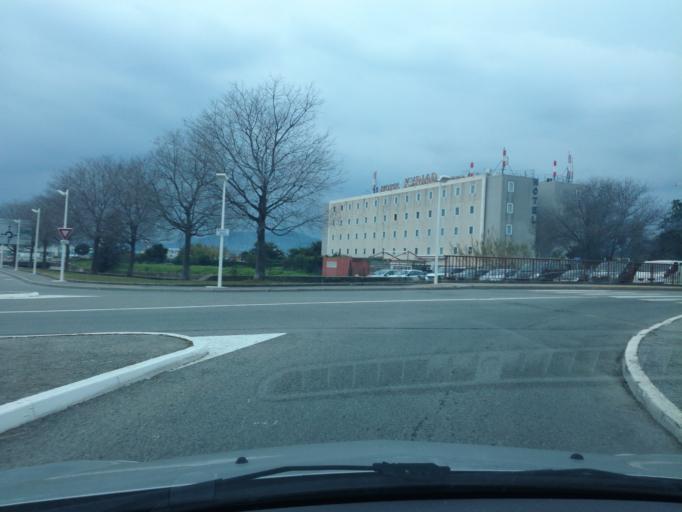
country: FR
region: Provence-Alpes-Cote d'Azur
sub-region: Departement des Alpes-Maritimes
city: Mandelieu-la-Napoule
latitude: 43.5515
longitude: 6.9620
